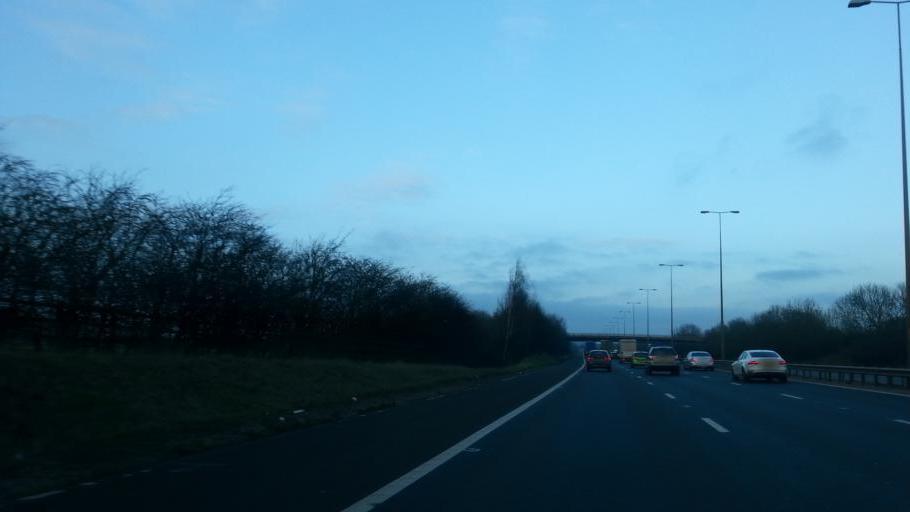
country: GB
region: England
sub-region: Worcestershire
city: Kempsey
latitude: 52.1375
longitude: -2.1977
